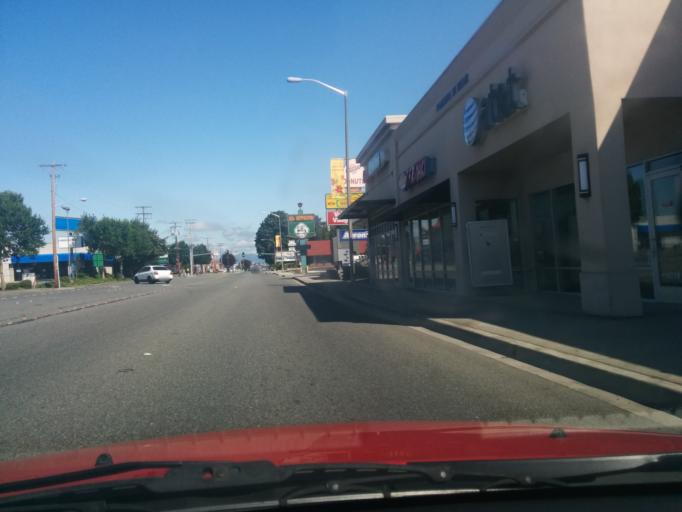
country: US
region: Washington
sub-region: Skagit County
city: Mount Vernon
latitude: 48.4365
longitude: -122.3350
